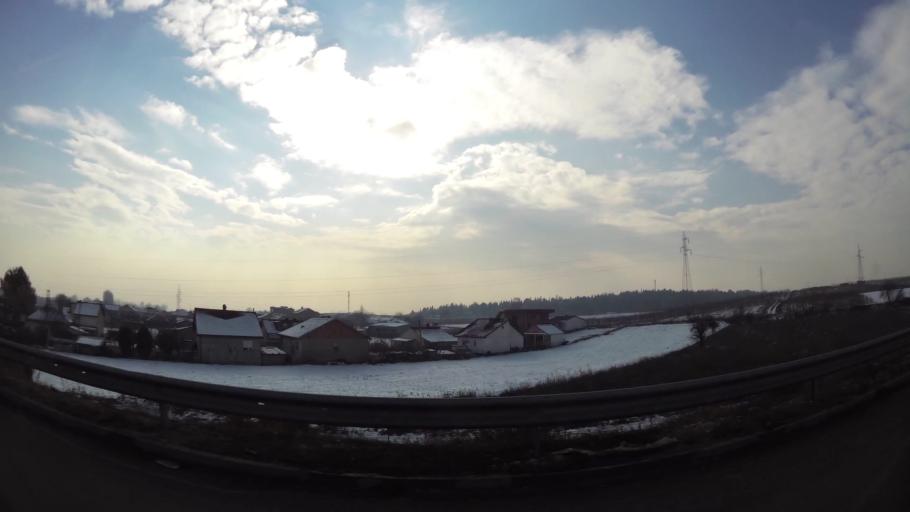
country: MK
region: Butel
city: Butel
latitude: 42.0452
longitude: 21.4419
